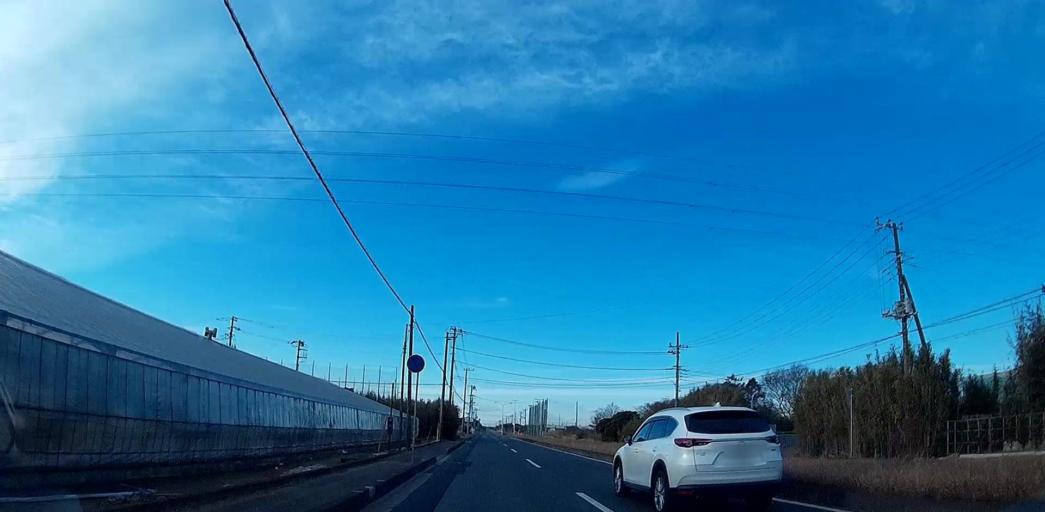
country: JP
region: Chiba
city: Hasaki
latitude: 35.8133
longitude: 140.7389
